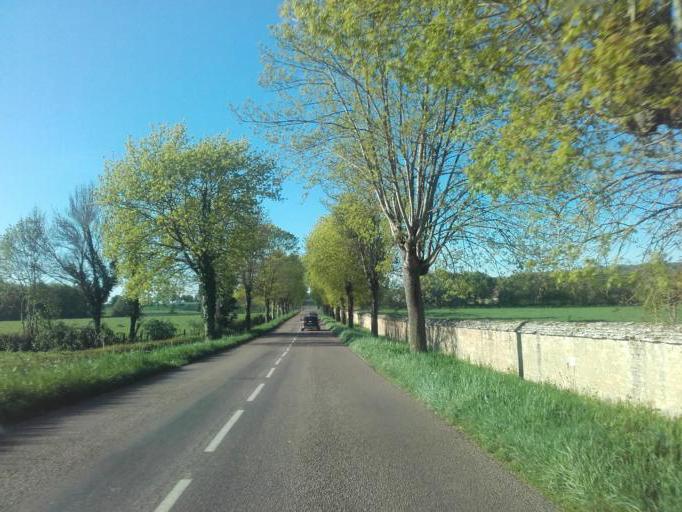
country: FR
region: Bourgogne
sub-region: Departement de Saone-et-Loire
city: Dracy-le-Fort
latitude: 46.8052
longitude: 4.7527
